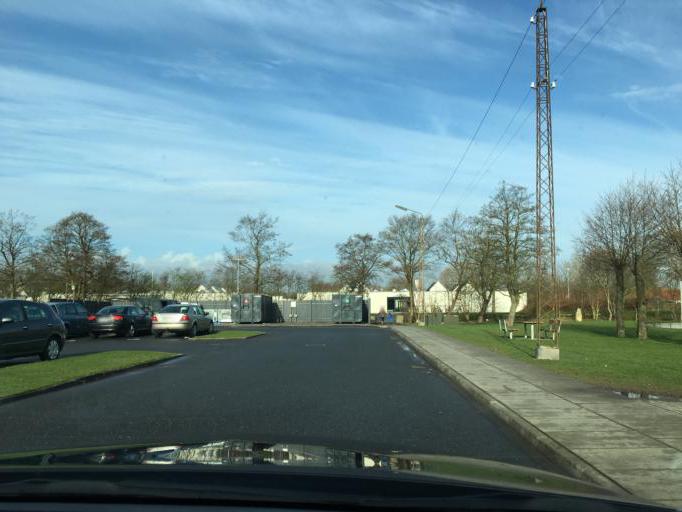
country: DK
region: South Denmark
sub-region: Kolding Kommune
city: Kolding
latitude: 55.5028
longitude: 9.4514
